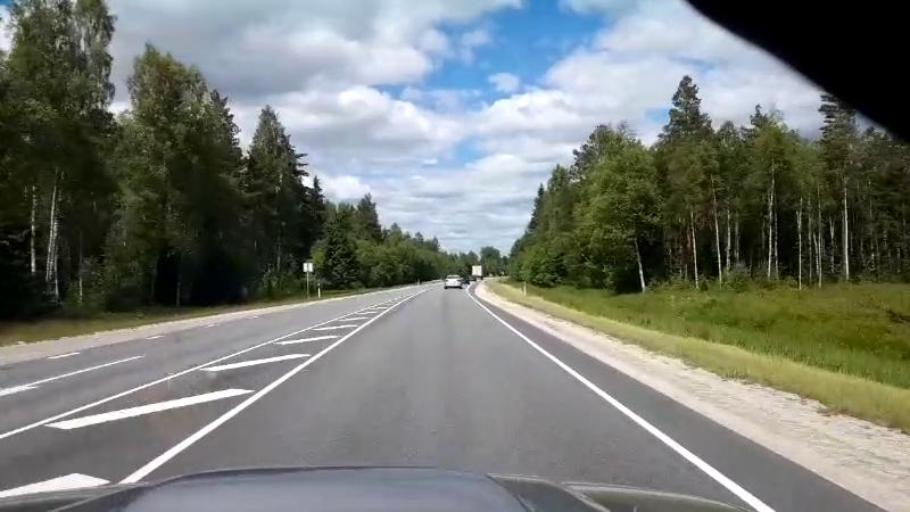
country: EE
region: Paernumaa
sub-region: Halinga vald
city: Parnu-Jaagupi
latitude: 58.7096
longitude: 24.4239
